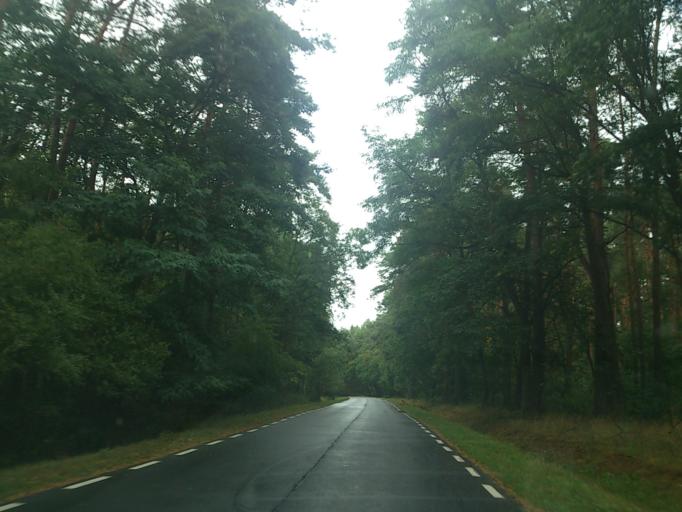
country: PL
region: Greater Poland Voivodeship
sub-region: Powiat poznanski
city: Pobiedziska
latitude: 52.5127
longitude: 17.1998
